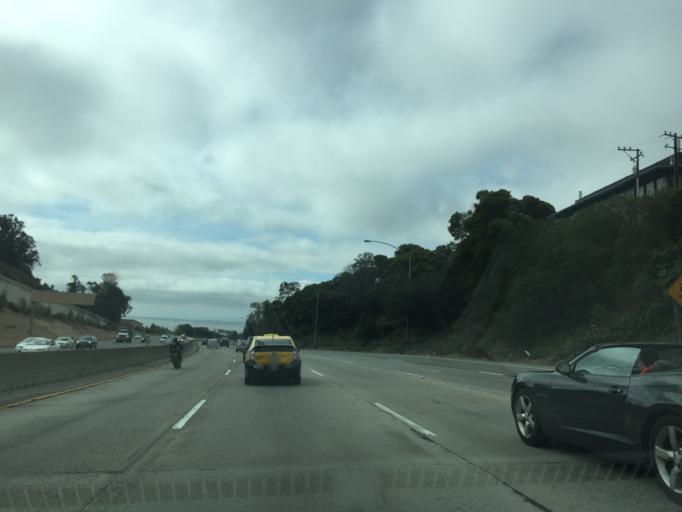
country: US
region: California
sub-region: San Mateo County
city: Brisbane
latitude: 37.7155
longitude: -122.3985
